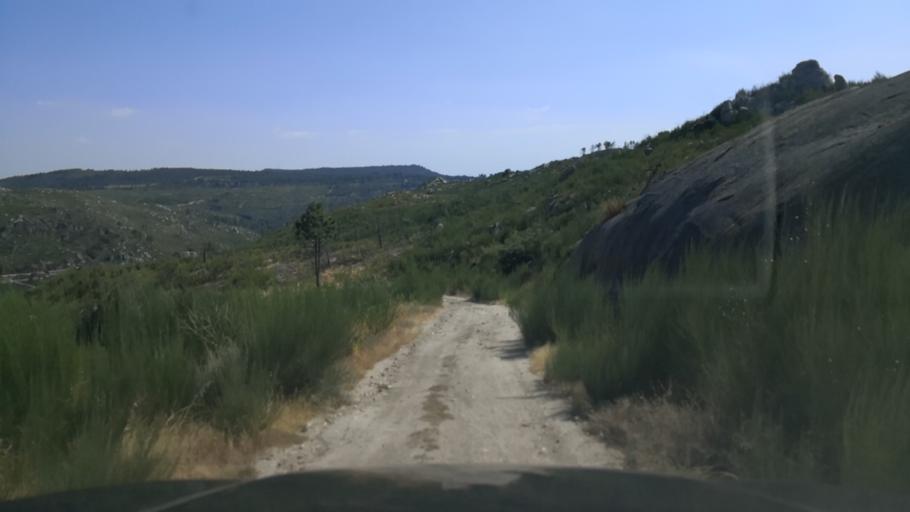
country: PT
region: Vila Real
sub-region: Sabrosa
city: Sabrosa
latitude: 41.3152
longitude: -7.4922
